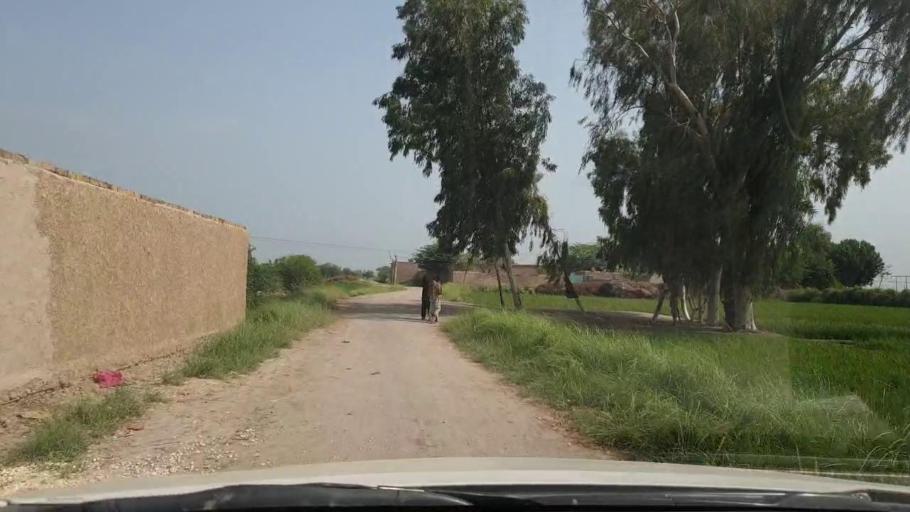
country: PK
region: Sindh
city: Shikarpur
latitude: 27.9741
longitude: 68.6704
